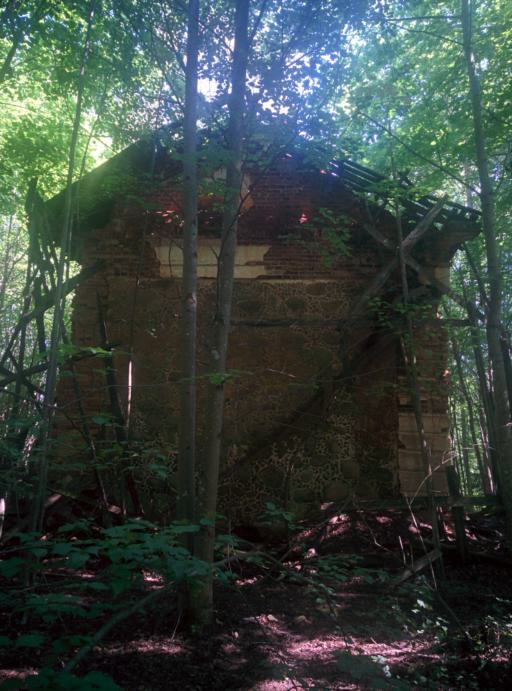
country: BY
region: Vitebsk
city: Pastavy
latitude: 55.0390
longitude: 26.8822
